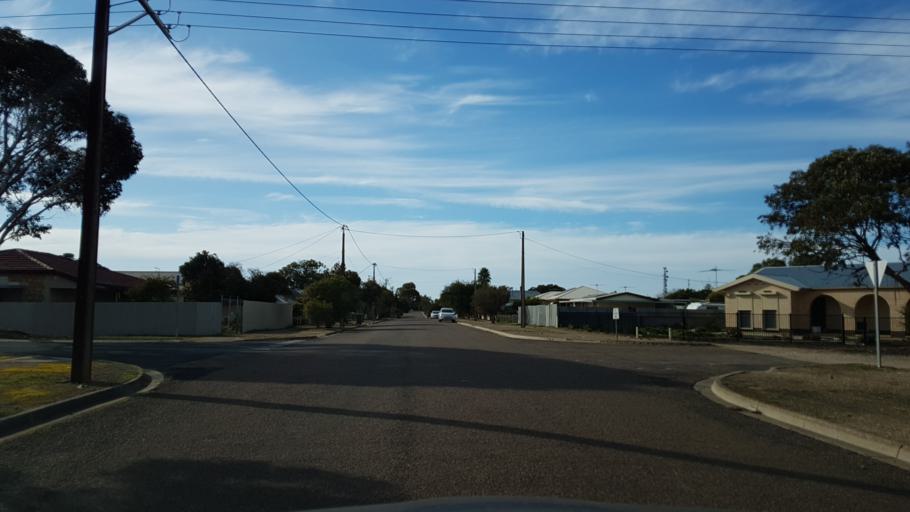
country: AU
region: South Australia
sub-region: Murray Bridge
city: Tailem Bend
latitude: -35.2528
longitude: 139.4575
